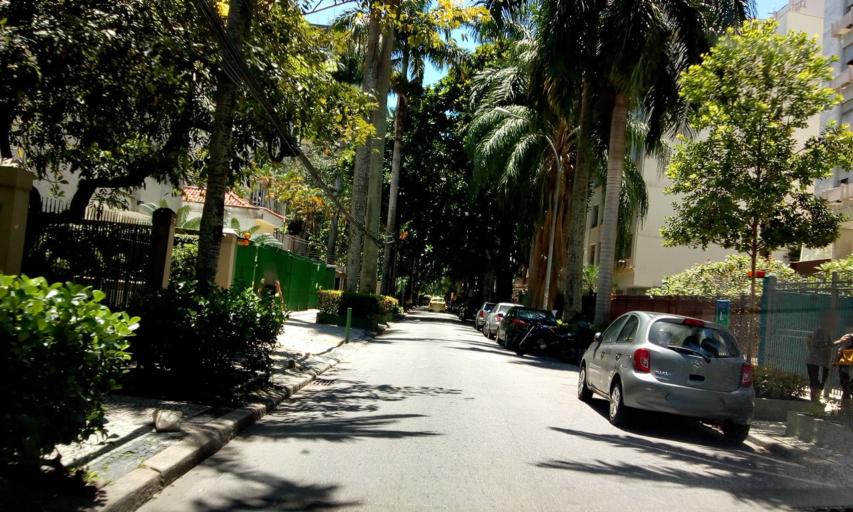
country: BR
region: Rio de Janeiro
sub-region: Rio De Janeiro
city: Rio de Janeiro
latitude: -22.9356
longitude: -43.1798
